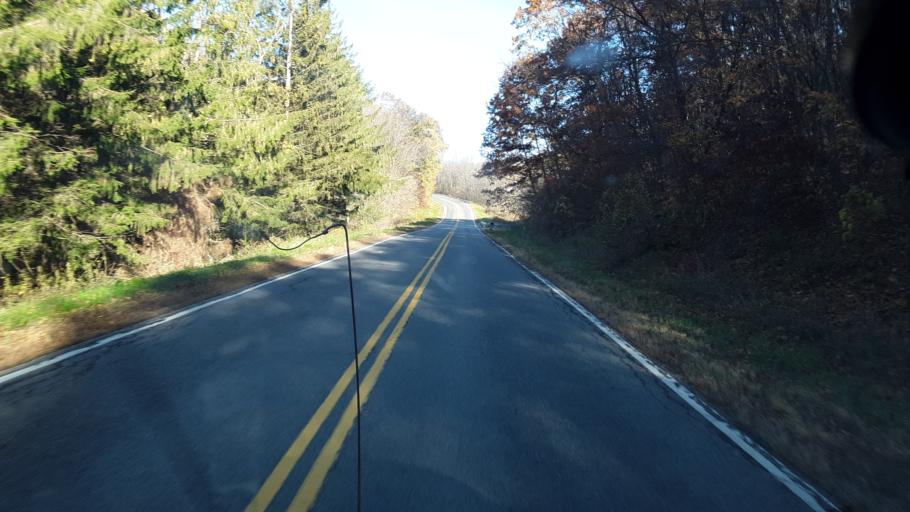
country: US
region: Wisconsin
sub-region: Vernon County
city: Hillsboro
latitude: 43.6629
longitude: -90.4455
